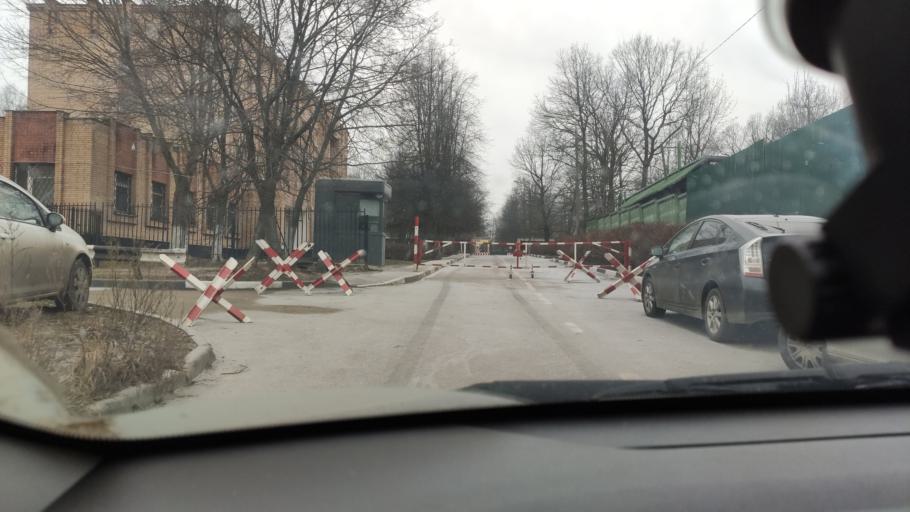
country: RU
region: Moscow
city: Chertanovo Yuzhnoye
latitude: 55.5892
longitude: 37.5881
